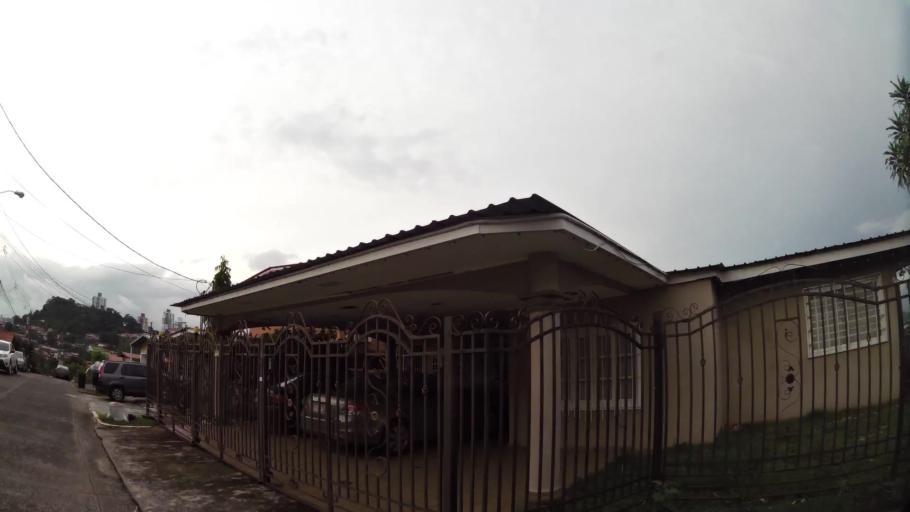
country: PA
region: Panama
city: Panama
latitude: 9.0181
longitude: -79.5258
